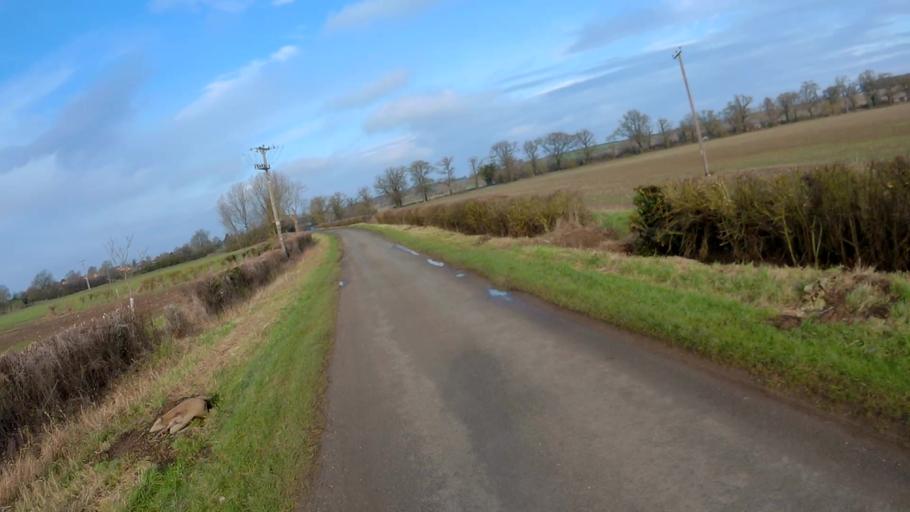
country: GB
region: England
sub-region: Lincolnshire
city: Bourne
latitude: 52.7743
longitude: -0.4259
